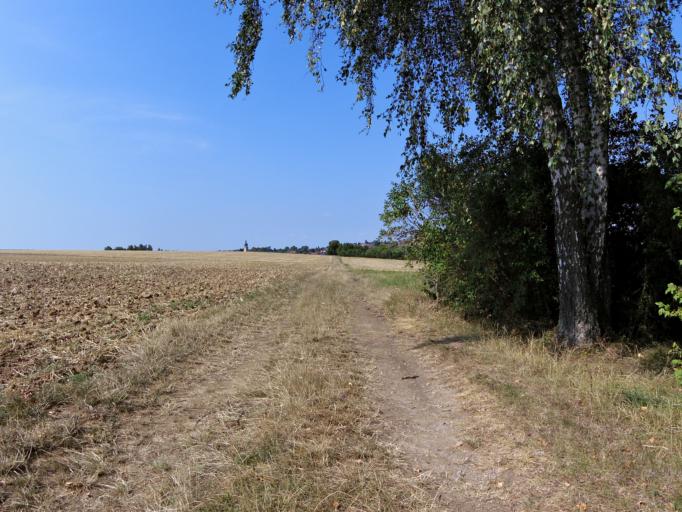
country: DE
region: Bavaria
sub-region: Regierungsbezirk Unterfranken
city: Estenfeld
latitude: 49.8322
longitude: 10.0199
